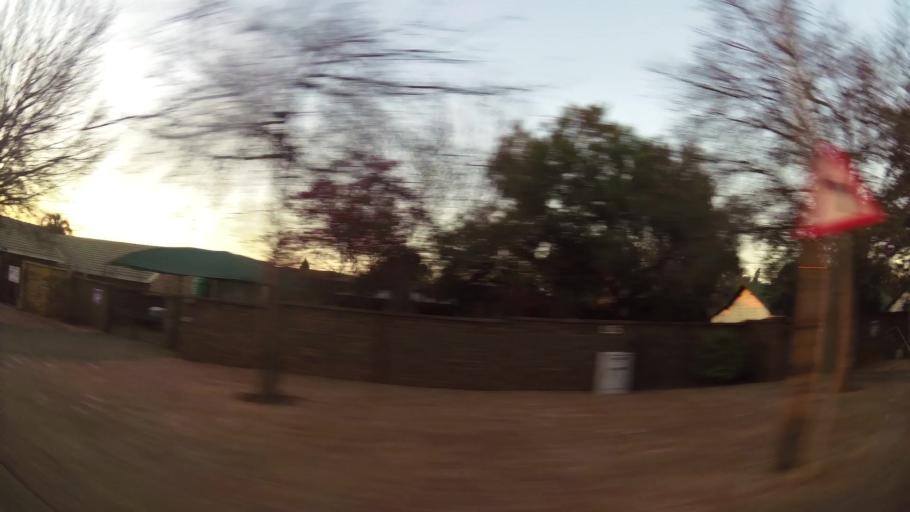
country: ZA
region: Gauteng
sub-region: City of Tshwane Metropolitan Municipality
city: Centurion
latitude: -25.8406
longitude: 28.1520
